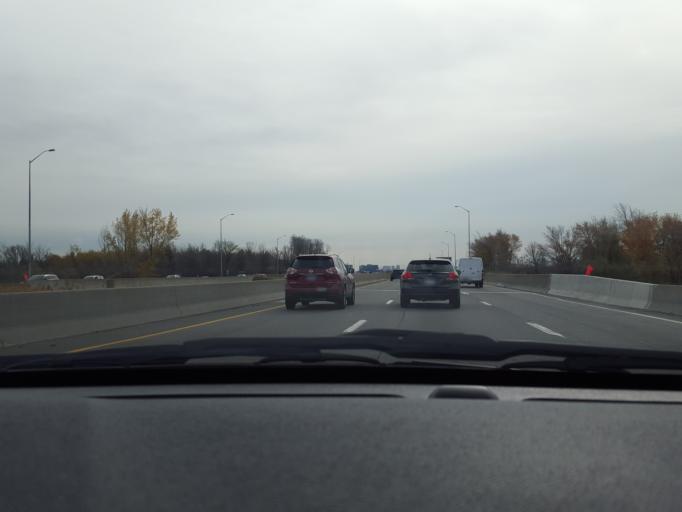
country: CA
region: Ontario
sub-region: York
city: Richmond Hill
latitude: 43.8748
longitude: -79.3780
